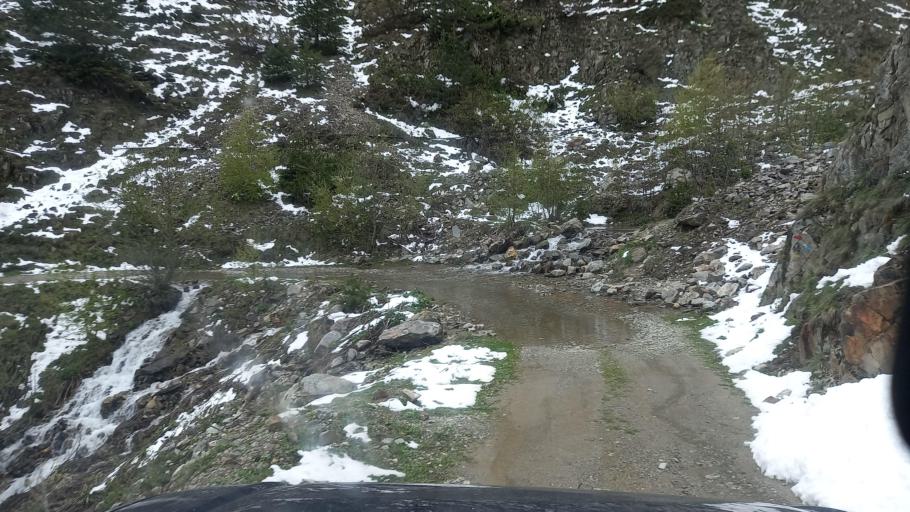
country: RU
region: North Ossetia
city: Mizur
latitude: 42.8034
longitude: 43.9335
